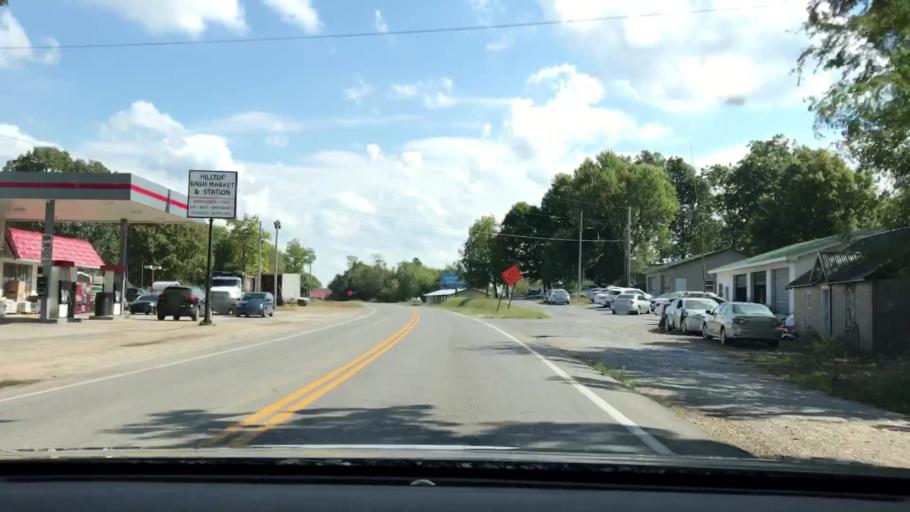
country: US
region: Kentucky
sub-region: Trigg County
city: Cadiz
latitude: 36.8109
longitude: -87.8910
